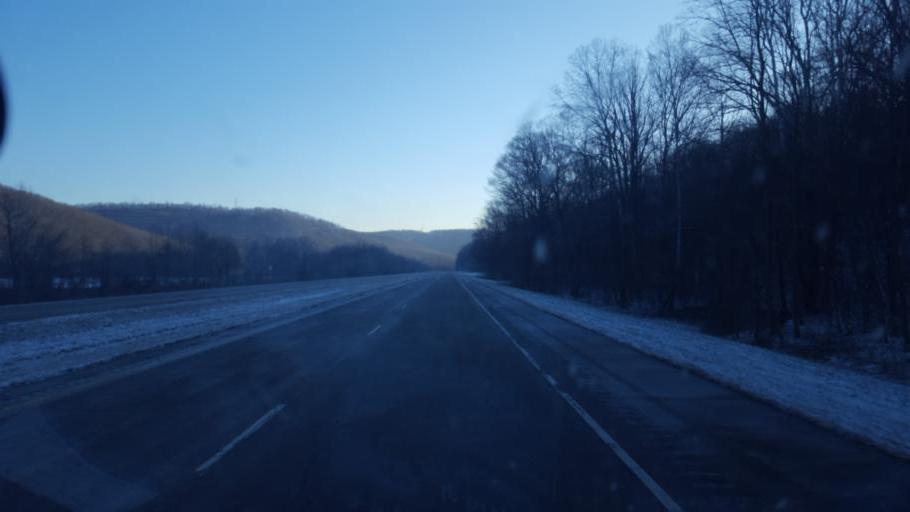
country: US
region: Ohio
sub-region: Pike County
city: Piketon
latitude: 39.0495
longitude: -83.2077
